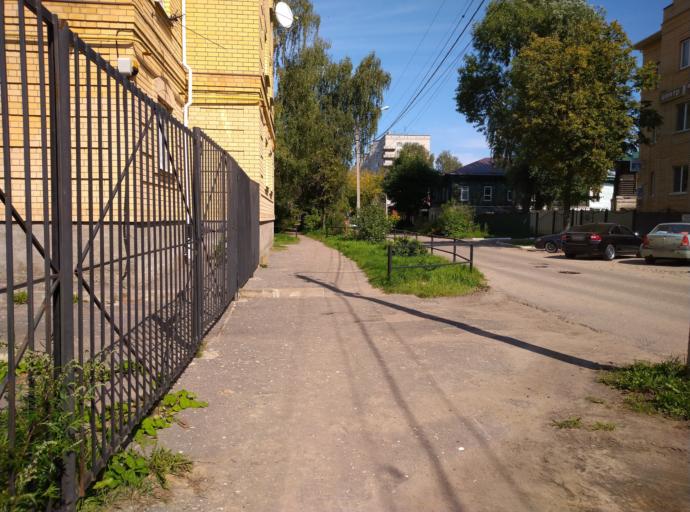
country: RU
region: Kostroma
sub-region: Kostromskoy Rayon
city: Kostroma
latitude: 57.7702
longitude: 40.9361
